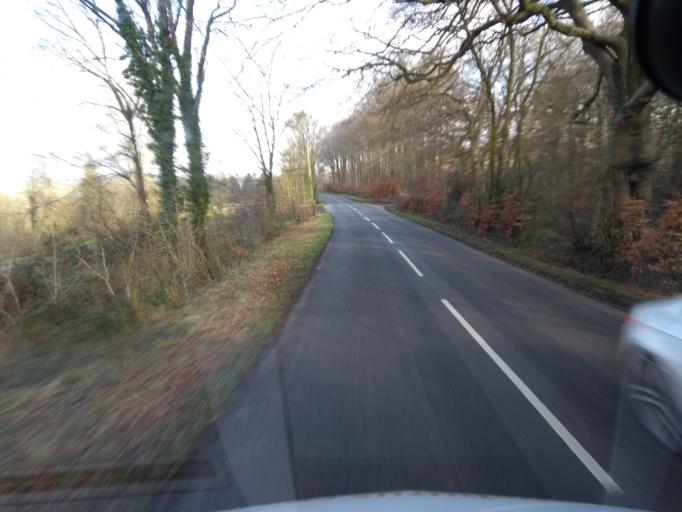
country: GB
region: England
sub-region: Somerset
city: Creech Saint Michael
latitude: 50.9372
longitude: -3.0452
